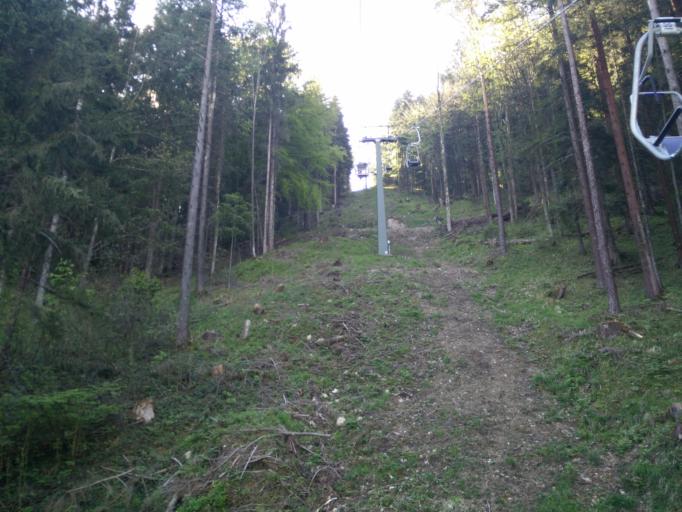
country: AT
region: Tyrol
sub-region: Politischer Bezirk Kufstein
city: Kufstein
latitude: 47.5893
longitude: 12.1881
